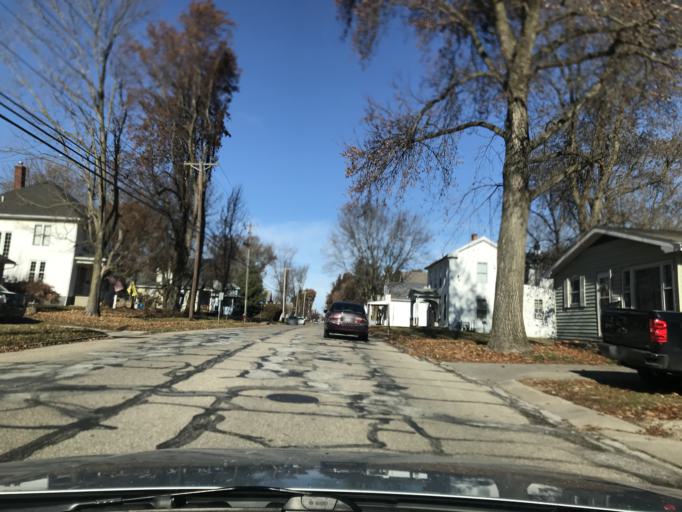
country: US
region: Illinois
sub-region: McDonough County
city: Macomb
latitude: 40.4526
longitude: -90.6673
